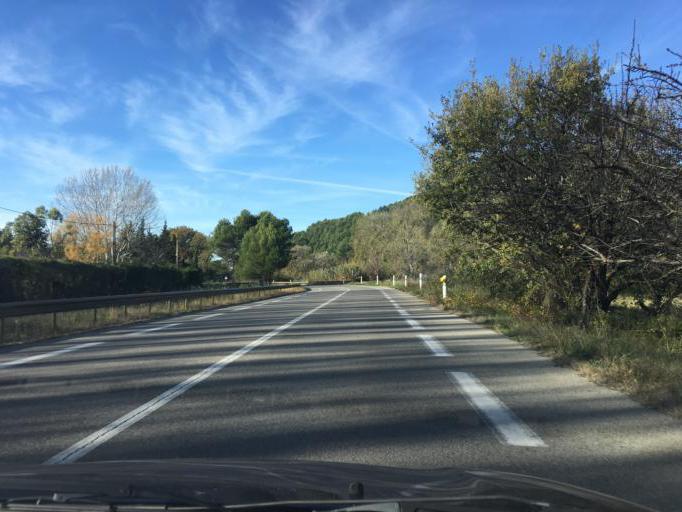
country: FR
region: Provence-Alpes-Cote d'Azur
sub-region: Departement des Bouches-du-Rhone
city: Mallemort
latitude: 43.7564
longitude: 5.1586
